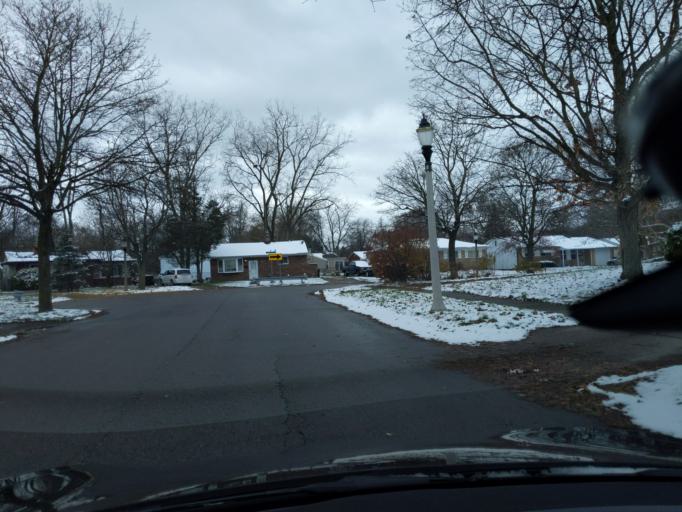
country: US
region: Michigan
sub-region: Eaton County
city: Waverly
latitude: 42.6867
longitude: -84.5945
